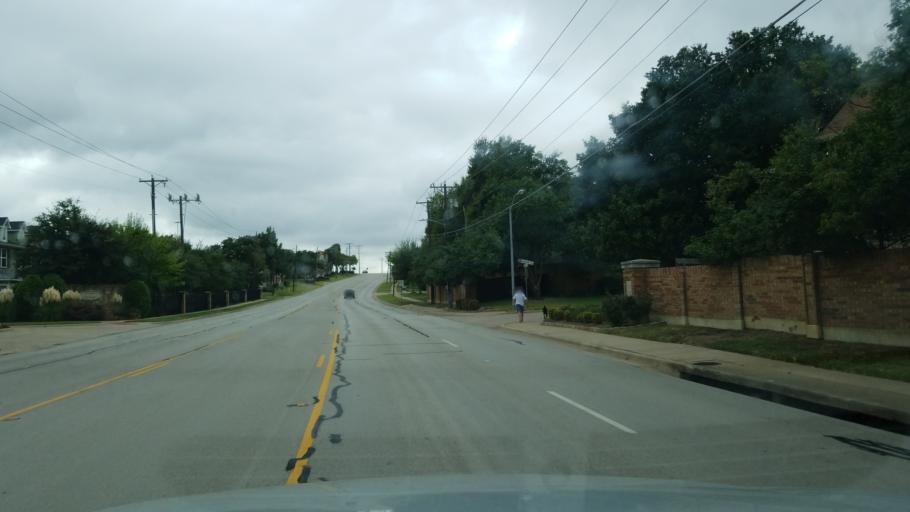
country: US
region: Texas
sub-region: Tarrant County
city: Euless
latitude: 32.8450
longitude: -97.1109
